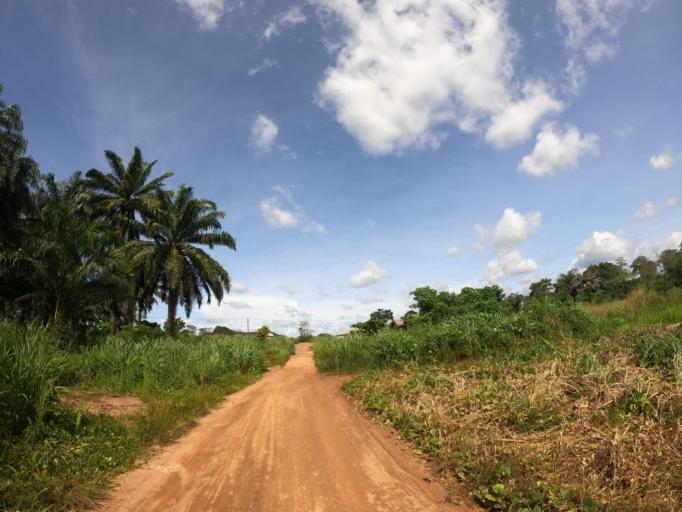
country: SL
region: Northern Province
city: Makeni
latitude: 8.8530
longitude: -12.0252
